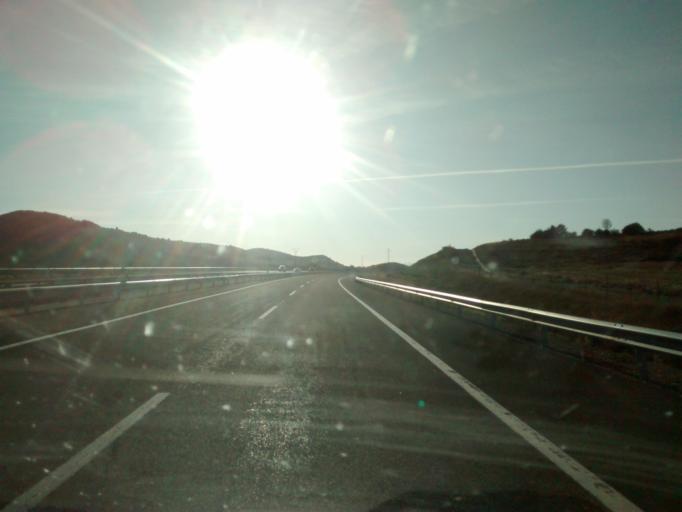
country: ES
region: Aragon
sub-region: Provincia de Huesca
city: Jaca
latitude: 42.5593
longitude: -0.4939
